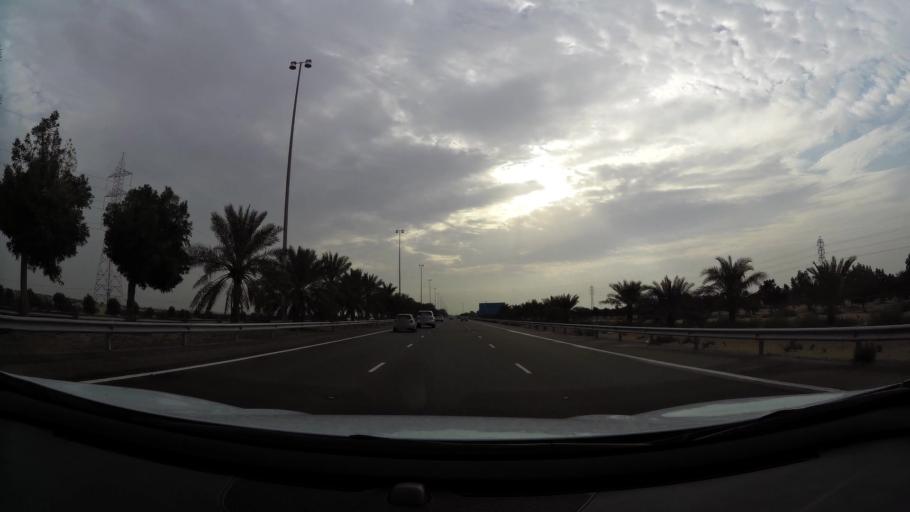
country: AE
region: Abu Dhabi
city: Abu Dhabi
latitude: 24.2256
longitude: 54.7992
